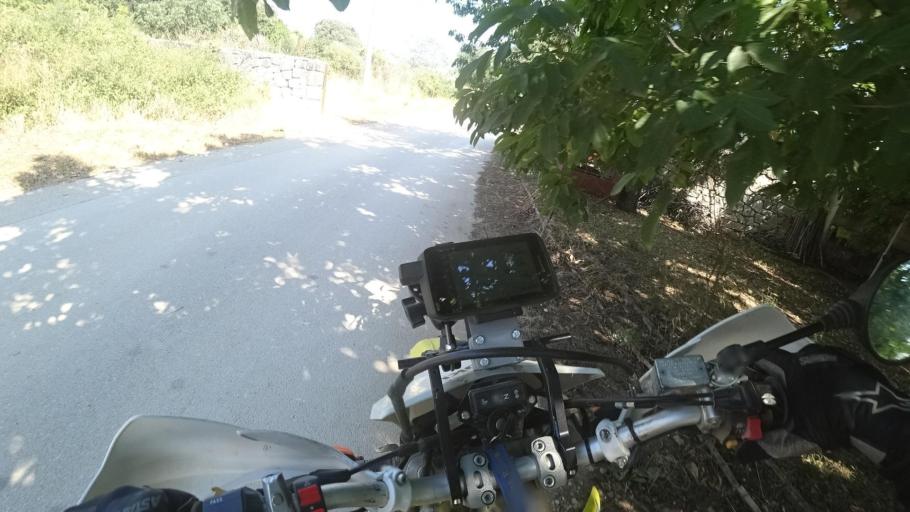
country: HR
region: Istarska
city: Fazana
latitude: 44.9924
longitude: 13.7421
